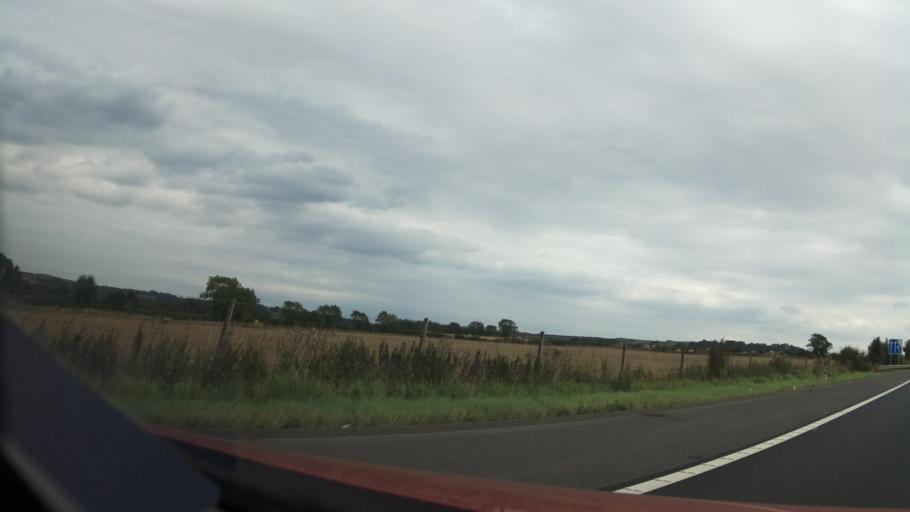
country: GB
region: England
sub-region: County Durham
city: Coxhoe
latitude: 54.7533
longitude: -1.5226
